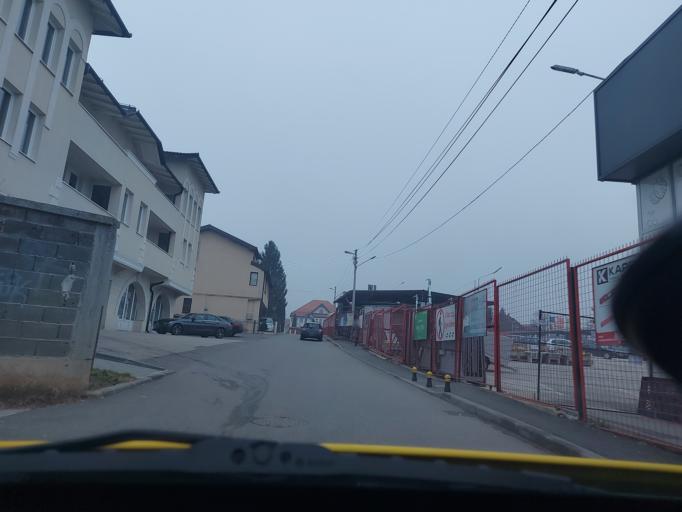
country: BA
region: Federation of Bosnia and Herzegovina
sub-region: Kanton Sarajevo
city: Sarajevo
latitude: 43.8392
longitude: 18.3327
